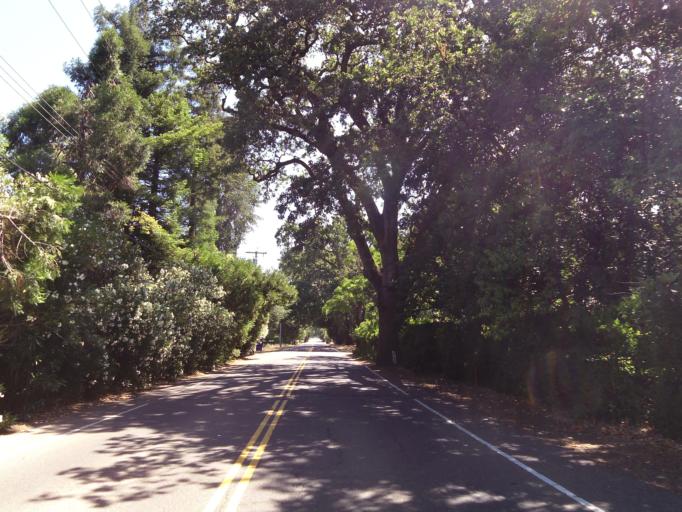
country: US
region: California
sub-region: Napa County
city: Saint Helena
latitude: 38.4878
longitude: -122.4356
